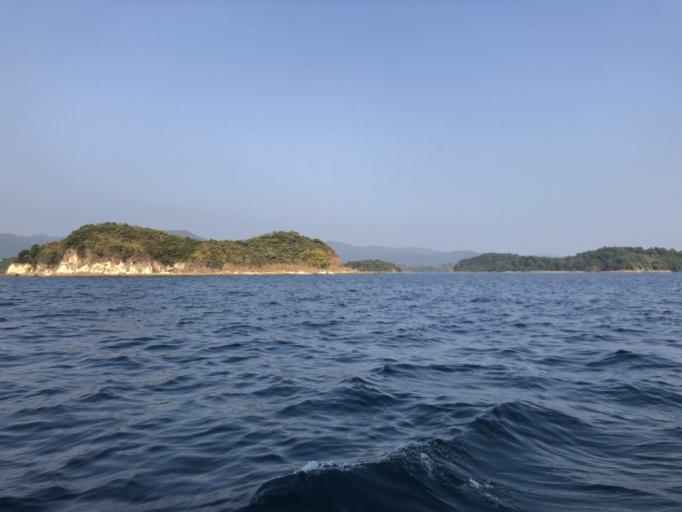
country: HK
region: Sai Kung
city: Sai Kung
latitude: 22.3724
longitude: 114.2831
